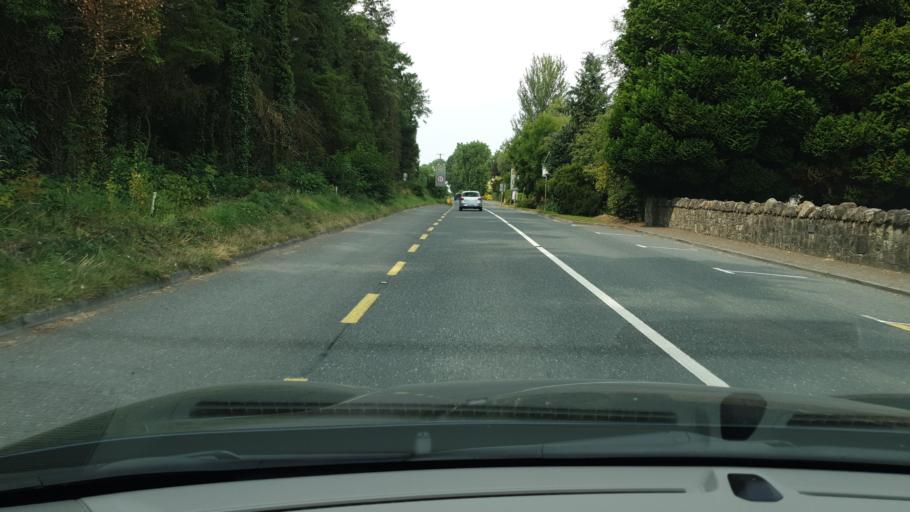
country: IE
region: Leinster
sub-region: An Mhi
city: Athboy
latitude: 53.6465
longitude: -6.8630
